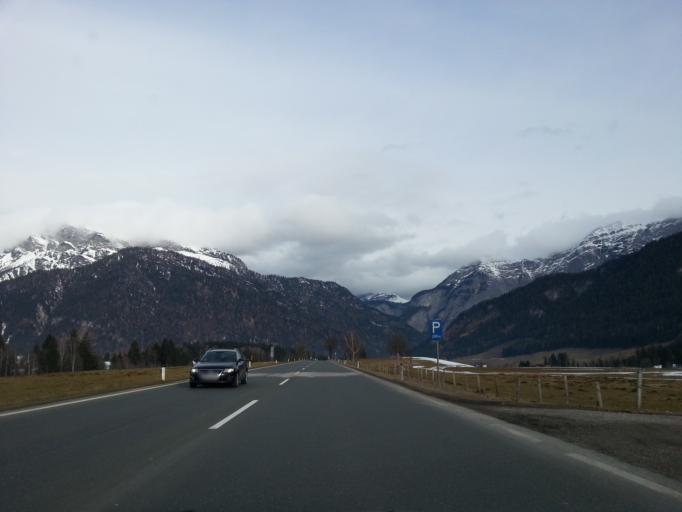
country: AT
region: Salzburg
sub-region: Politischer Bezirk Zell am See
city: Saalfelden am Steinernen Meer
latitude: 47.4401
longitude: 12.8408
